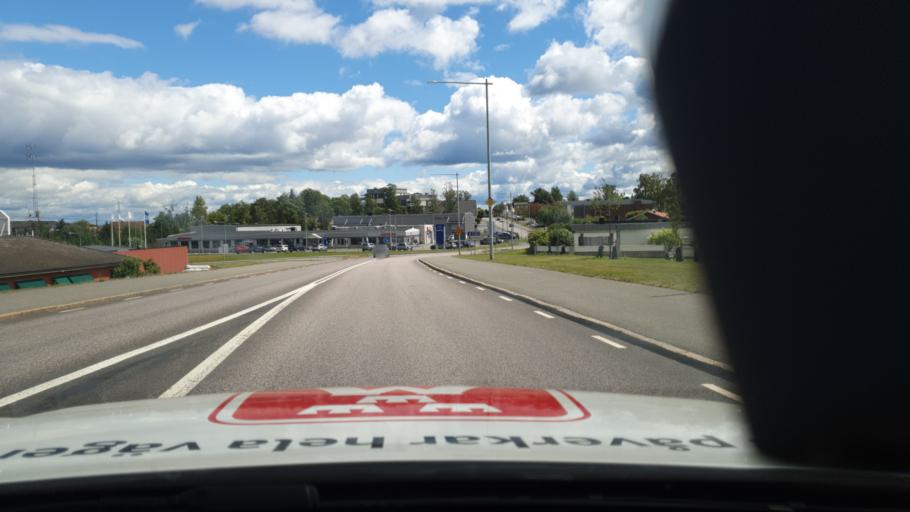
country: SE
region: Joenkoeping
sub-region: Habo Kommun
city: Habo
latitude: 57.9085
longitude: 14.0682
